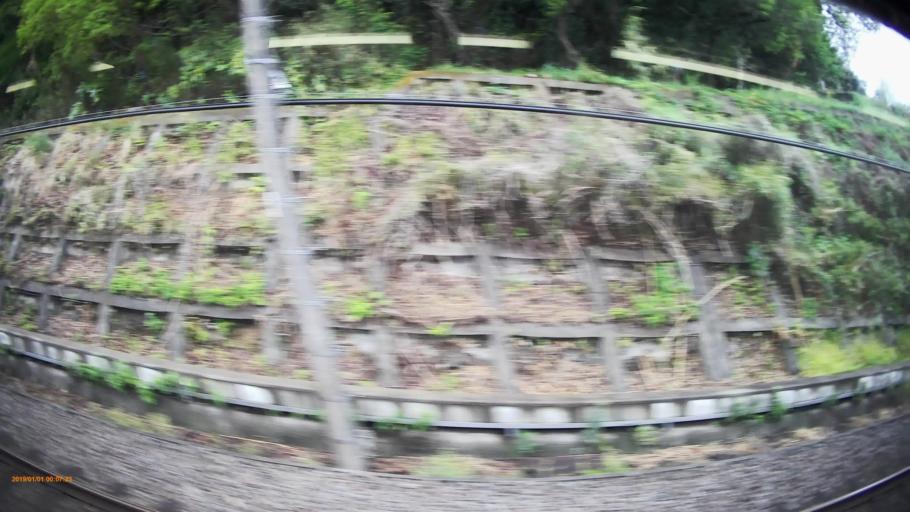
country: JP
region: Tokyo
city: Hachioji
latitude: 35.6418
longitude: 139.2699
